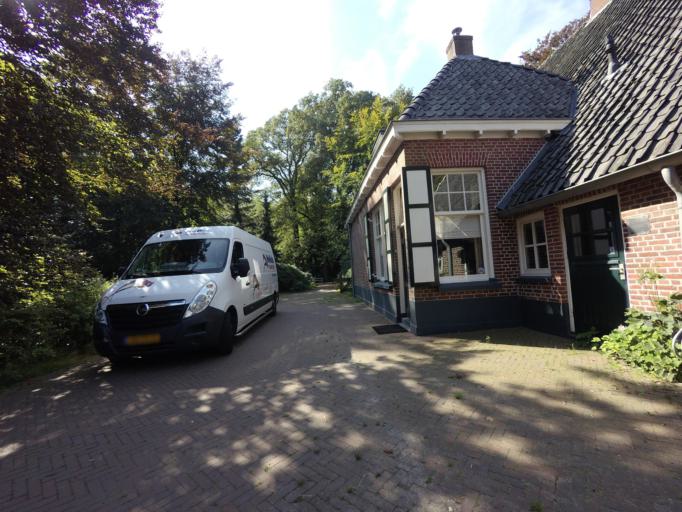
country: NL
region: Overijssel
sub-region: Gemeente Enschede
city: Enschede
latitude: 52.1862
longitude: 6.8932
